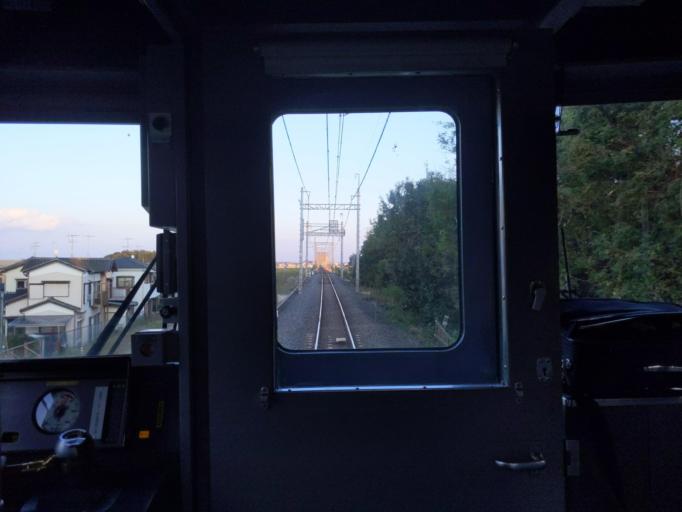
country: JP
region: Chiba
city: Noda
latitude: 35.9804
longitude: 139.8208
